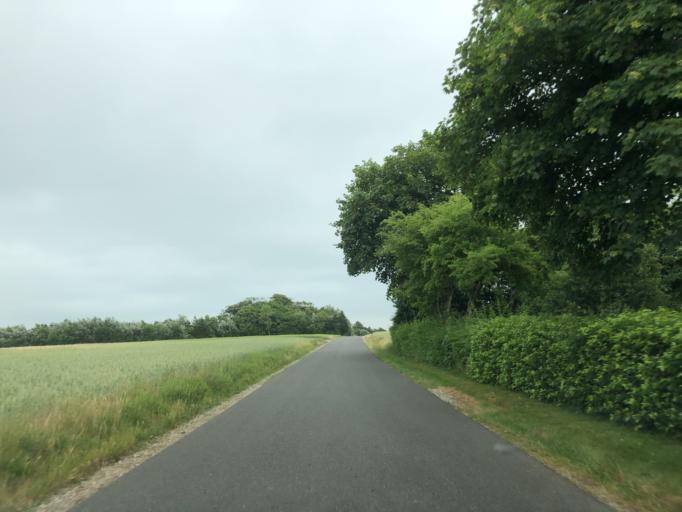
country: DK
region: Central Jutland
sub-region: Holstebro Kommune
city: Holstebro
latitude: 56.2547
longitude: 8.5753
